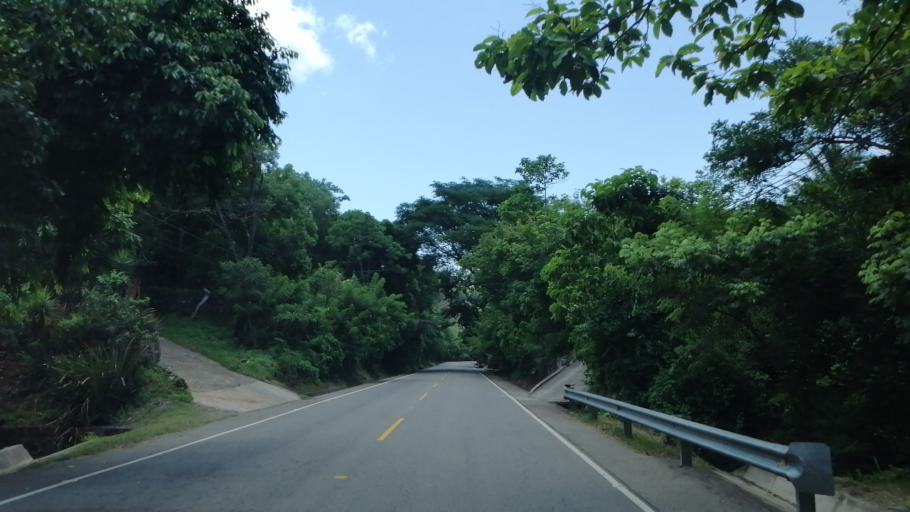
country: SV
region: Chalatenango
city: Nueva Concepcion
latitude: 14.1824
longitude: -89.3254
